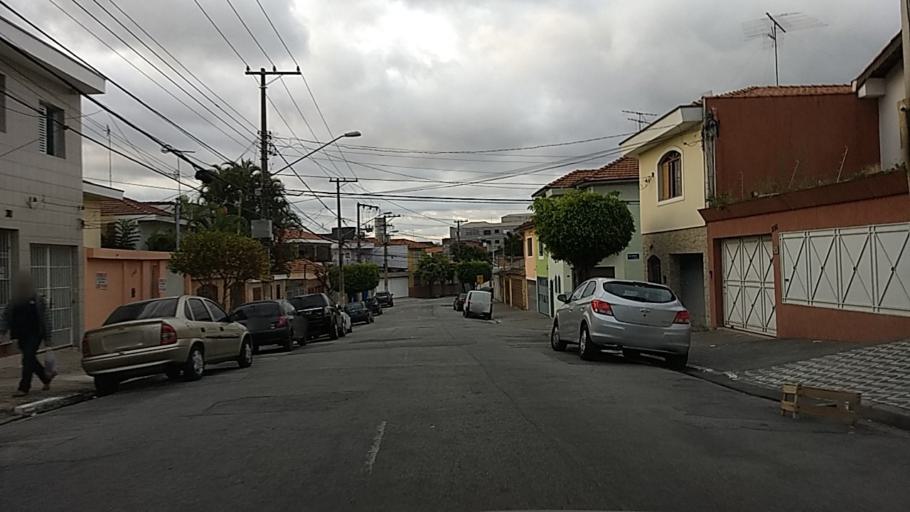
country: BR
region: Sao Paulo
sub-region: Sao Paulo
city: Sao Paulo
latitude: -23.5271
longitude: -46.6153
